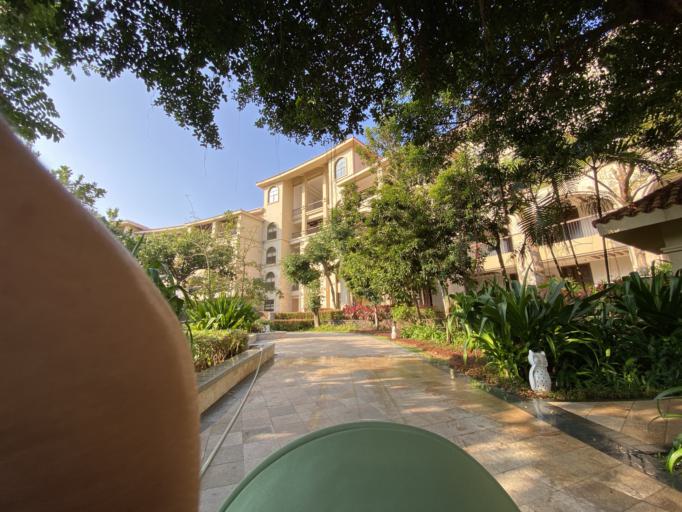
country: CN
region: Hainan
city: Haitangwan
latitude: 18.3497
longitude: 109.7386
